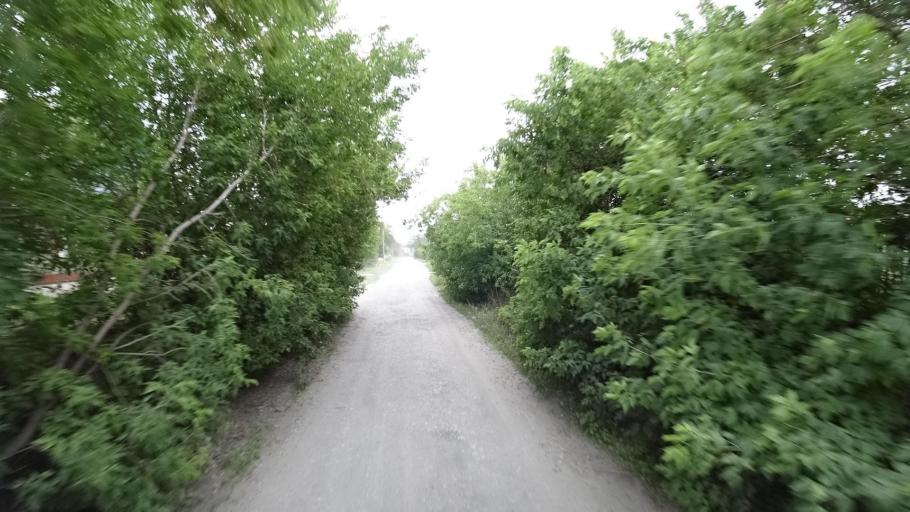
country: RU
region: Sverdlovsk
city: Kamyshlov
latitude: 56.8489
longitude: 62.6794
